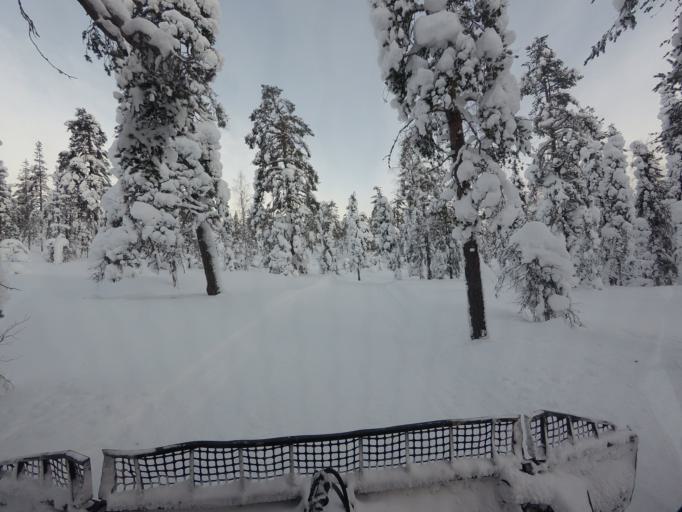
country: FI
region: Lapland
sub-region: Tunturi-Lappi
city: Kolari
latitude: 67.6507
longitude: 24.2415
